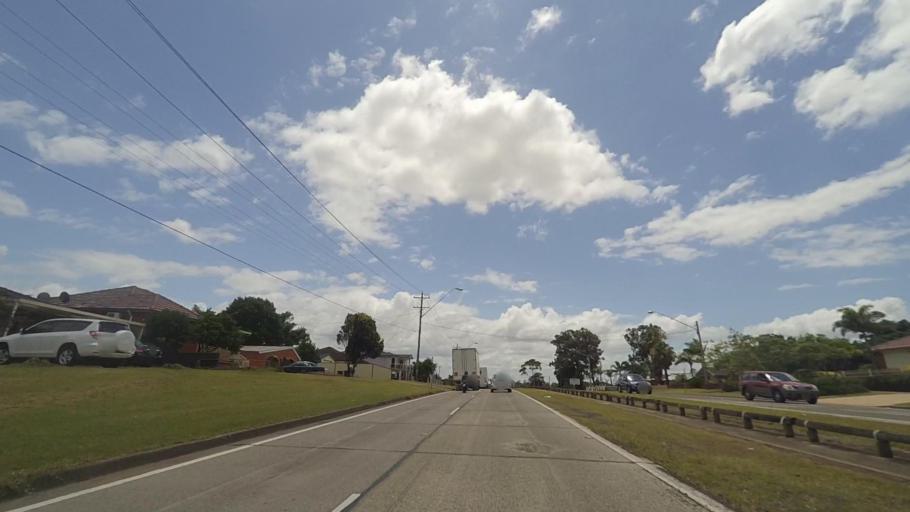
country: AU
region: New South Wales
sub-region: Fairfield
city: Fairfield Heights
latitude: -33.8658
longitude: 150.9259
